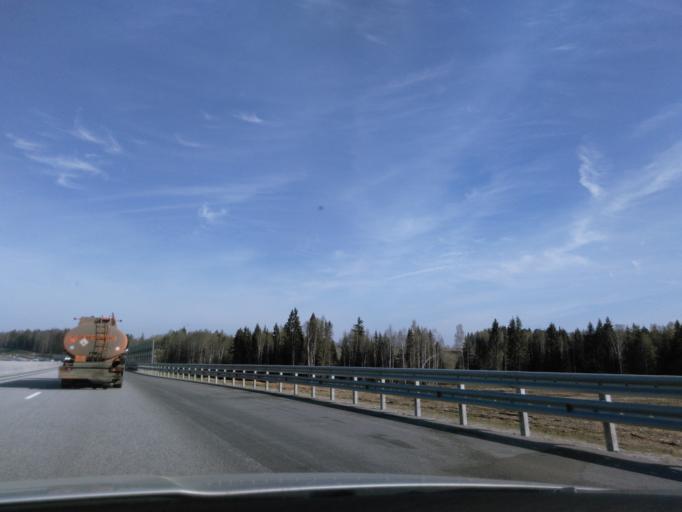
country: RU
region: Moskovskaya
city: Mendeleyevo
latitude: 56.0868
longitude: 37.2044
